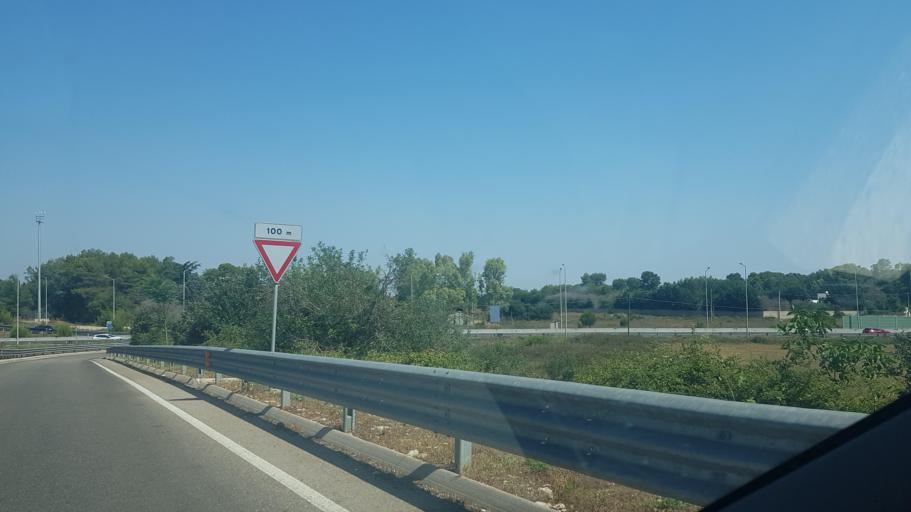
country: IT
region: Apulia
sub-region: Provincia di Lecce
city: Maglie
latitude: 40.1216
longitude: 18.3174
